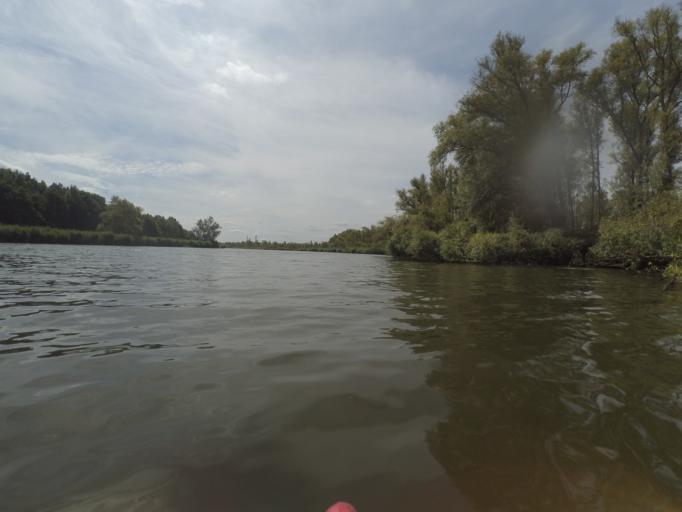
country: NL
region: North Brabant
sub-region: Gemeente Geertruidenberg
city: Geertruidenberg
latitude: 51.7461
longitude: 4.8498
